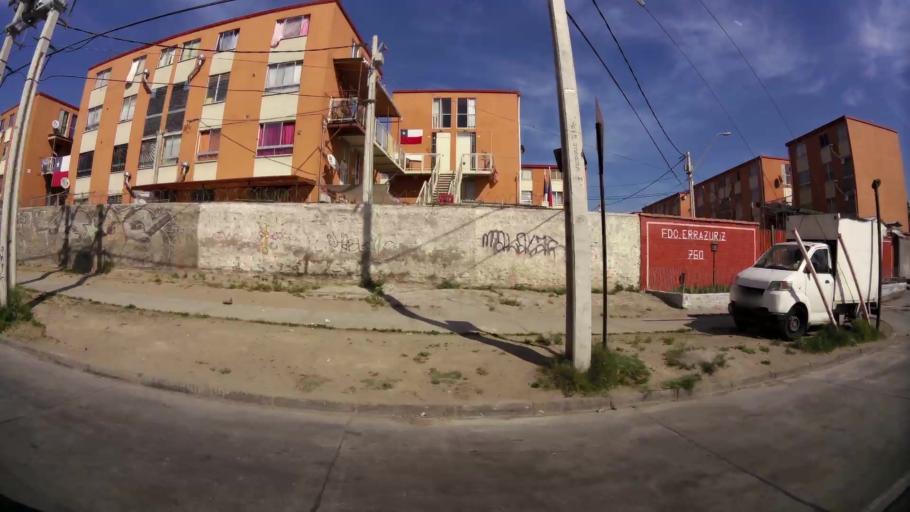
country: CL
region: Santiago Metropolitan
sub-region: Provincia de Santiago
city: Lo Prado
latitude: -33.4437
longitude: -70.7638
